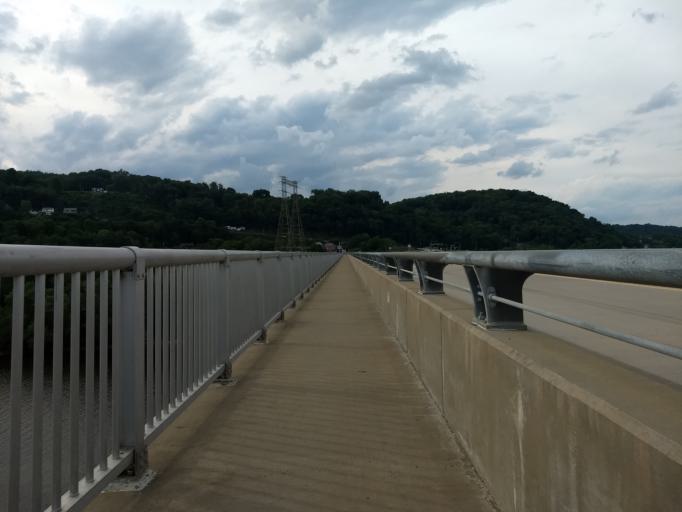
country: US
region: Pennsylvania
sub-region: Armstrong County
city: Freeport
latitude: 40.6678
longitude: -79.6918
